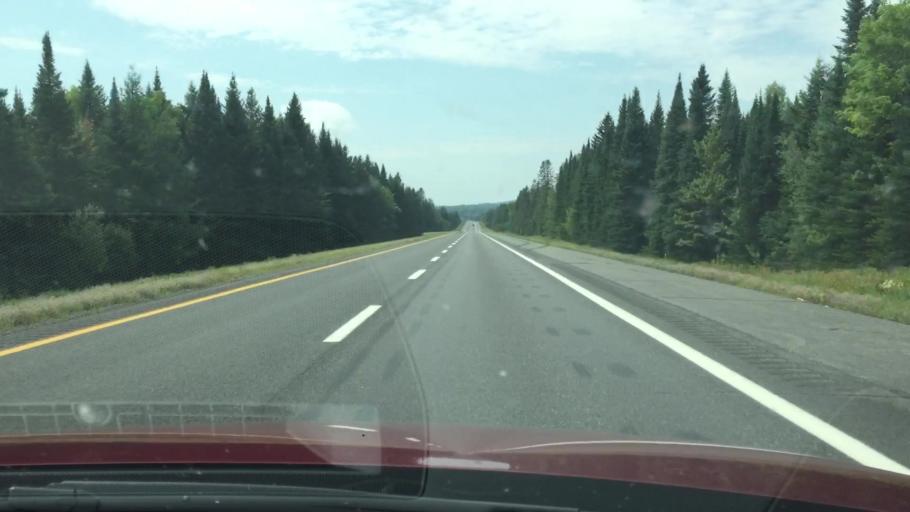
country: US
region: Maine
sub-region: Aroostook County
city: Hodgdon
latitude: 46.1161
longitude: -68.1363
